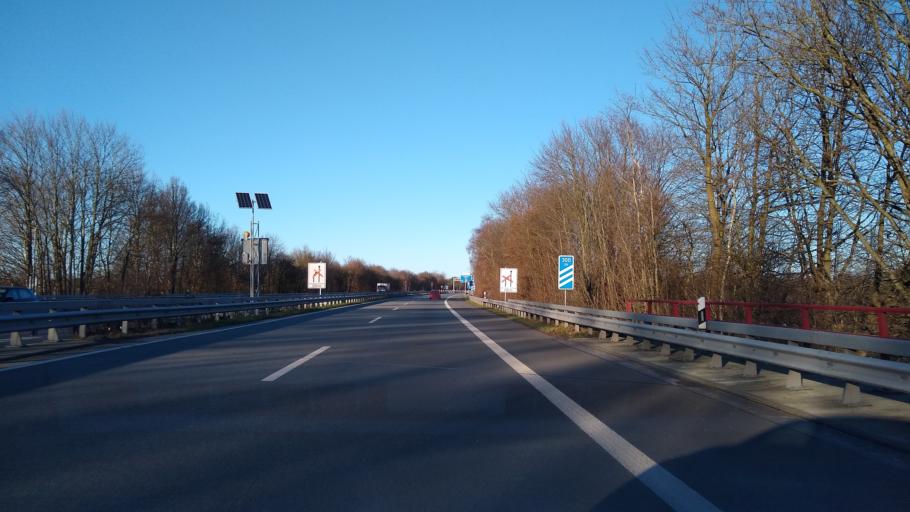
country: DE
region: Lower Saxony
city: Rastede
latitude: 53.2018
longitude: 8.2209
